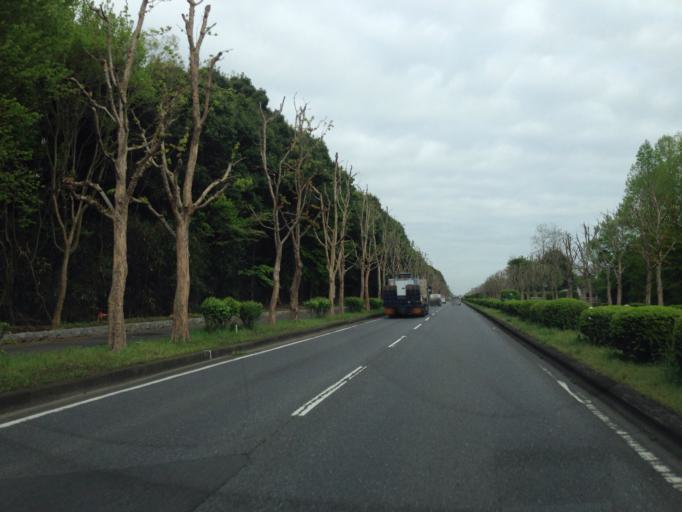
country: JP
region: Ibaraki
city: Tsukuba
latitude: 36.1191
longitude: 140.1003
